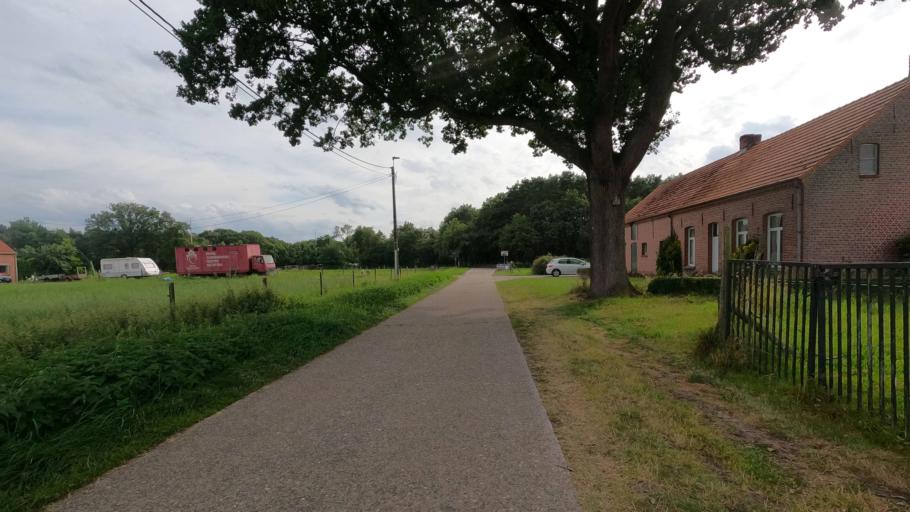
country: BE
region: Flanders
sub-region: Provincie Antwerpen
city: Lille
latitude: 51.2533
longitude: 4.7948
